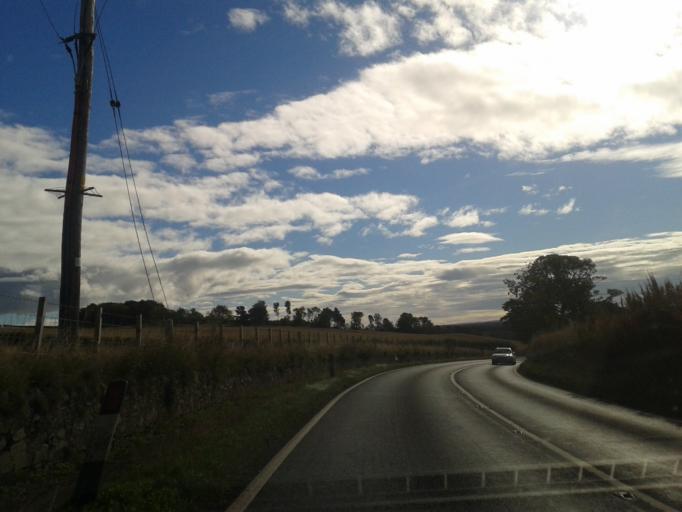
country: GB
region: Scotland
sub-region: Fife
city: Newport-On-Tay
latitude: 56.4264
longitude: -2.9259
